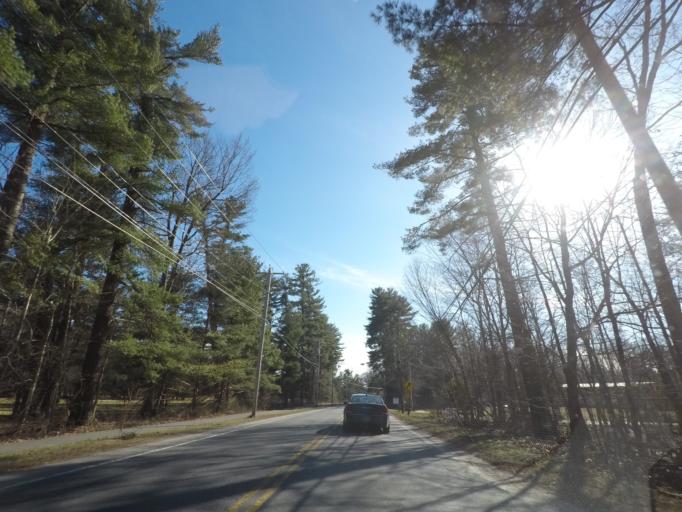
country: US
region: New York
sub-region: Saratoga County
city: Saratoga Springs
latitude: 43.0636
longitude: -73.7993
